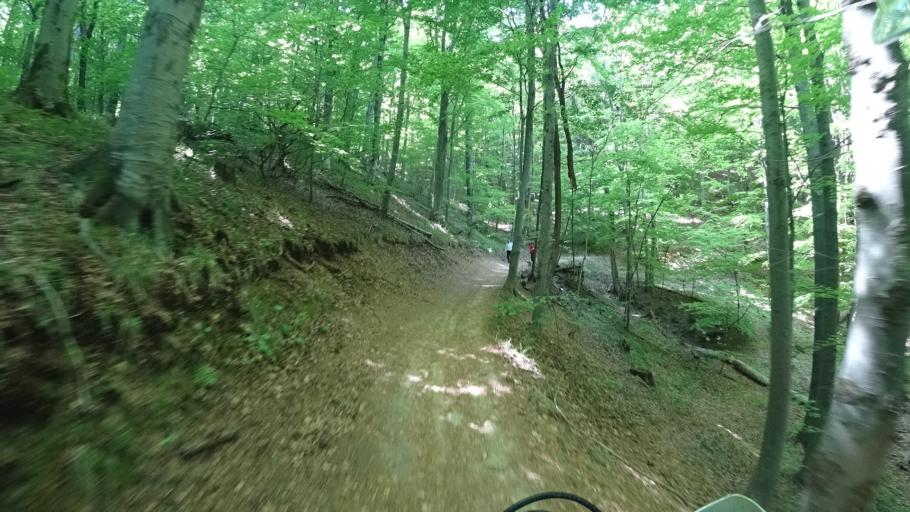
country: HR
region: Zagrebacka
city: Jablanovec
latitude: 45.8775
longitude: 15.8967
